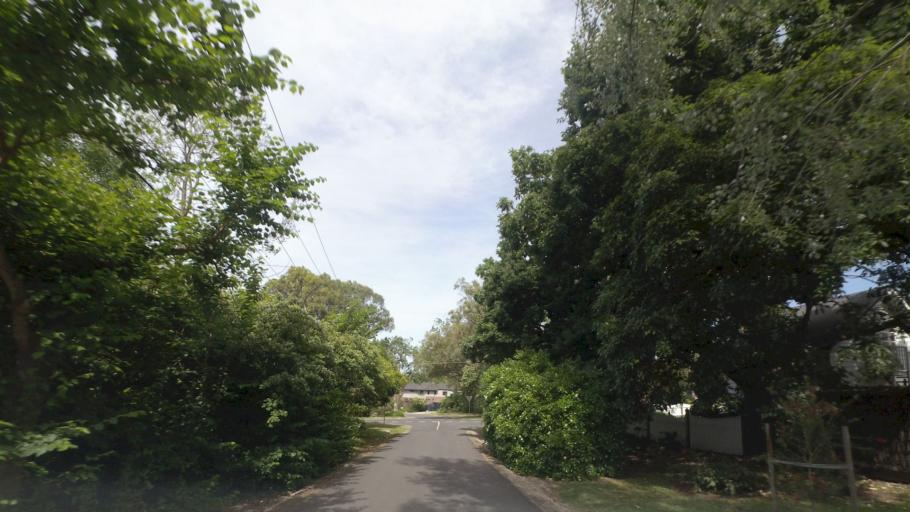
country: AU
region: Victoria
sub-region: Maroondah
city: Croydon North
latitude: -37.7841
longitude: 145.2961
